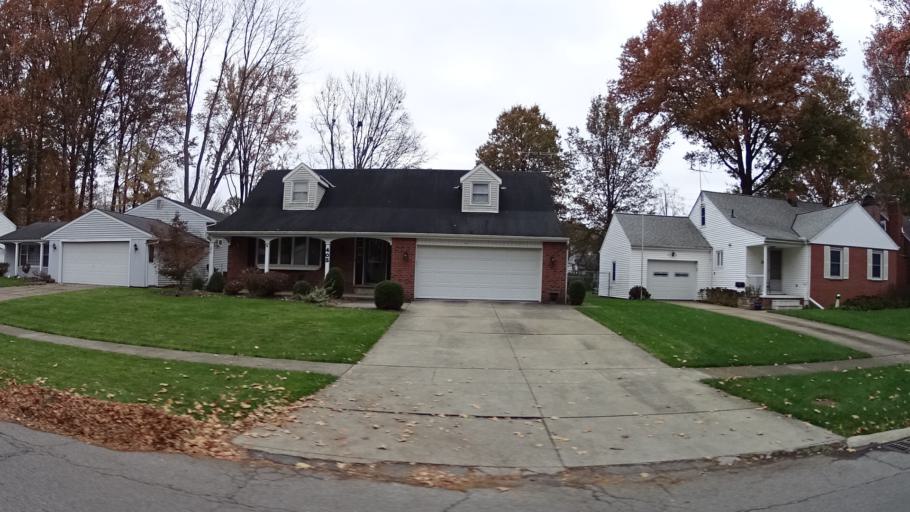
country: US
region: Ohio
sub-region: Lorain County
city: Elyria
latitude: 41.3542
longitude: -82.0913
